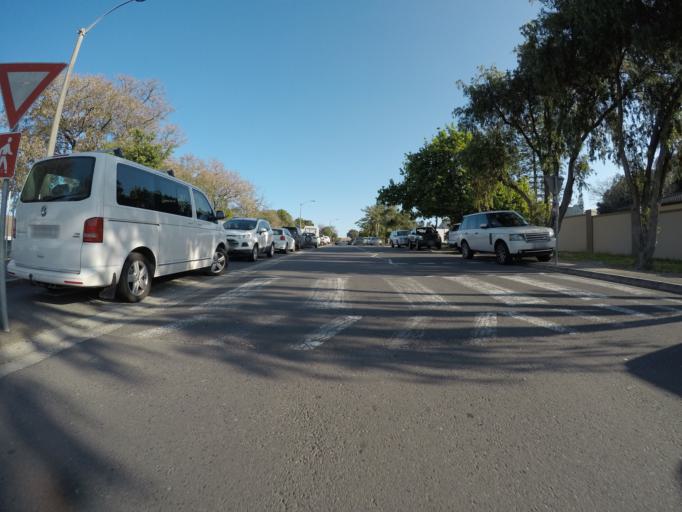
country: ZA
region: Western Cape
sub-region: City of Cape Town
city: Kraaifontein
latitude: -33.8536
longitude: 18.6576
